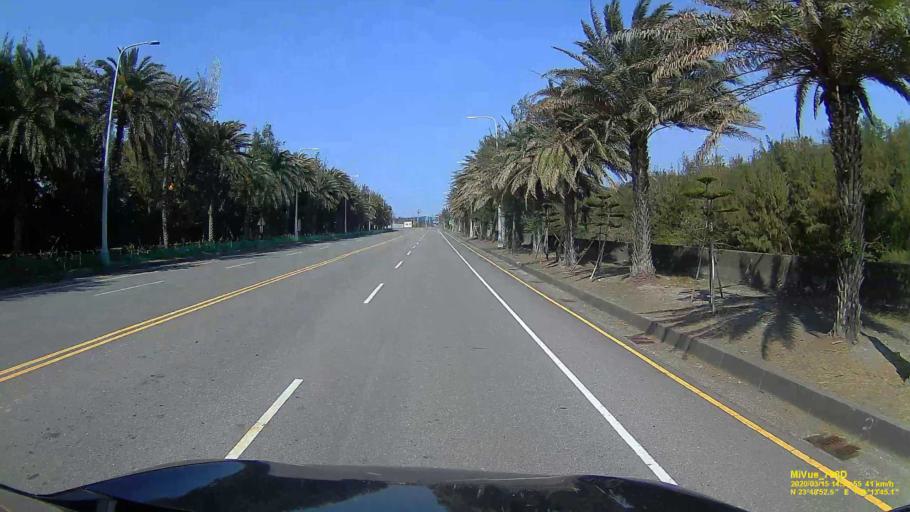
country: TW
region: Taiwan
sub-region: Yunlin
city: Douliu
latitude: 23.8148
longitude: 120.2293
